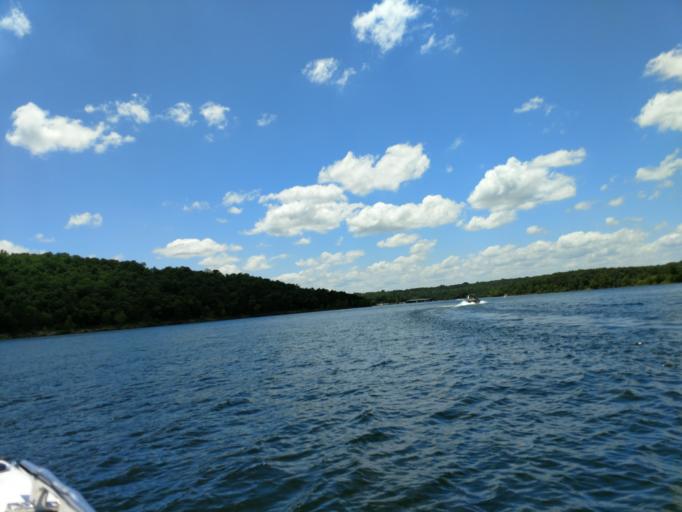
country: US
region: Missouri
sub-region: Barry County
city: Shell Knob
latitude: 36.5918
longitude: -93.5396
